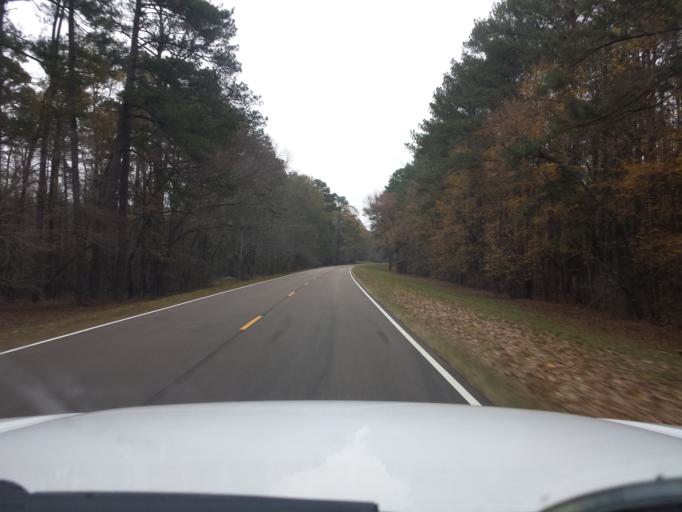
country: US
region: Mississippi
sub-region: Madison County
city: Canton
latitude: 32.5368
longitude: -89.9584
